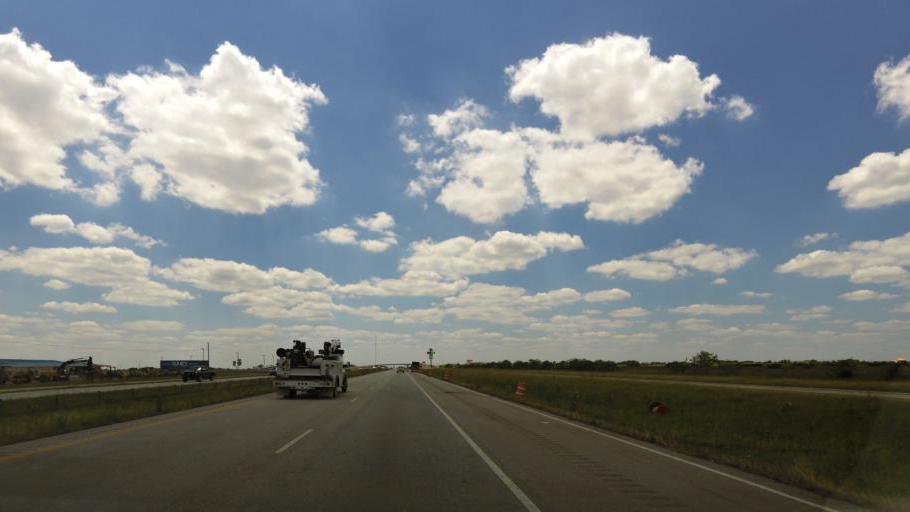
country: US
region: Texas
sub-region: Colorado County
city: Eagle Lake
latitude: 29.7433
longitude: -96.3221
